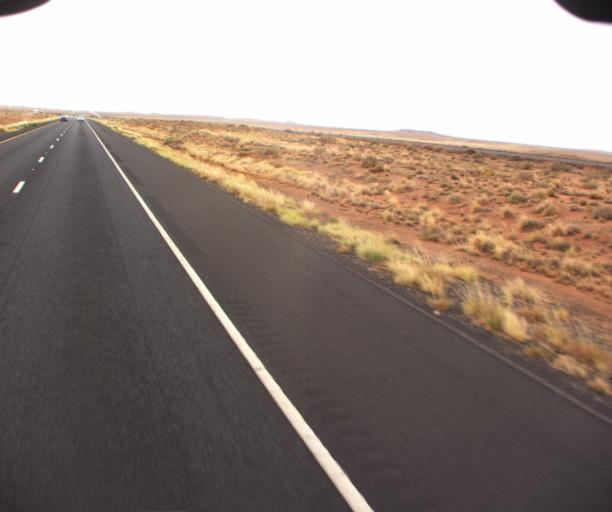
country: US
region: Arizona
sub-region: Coconino County
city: LeChee
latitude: 35.0577
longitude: -110.8026
